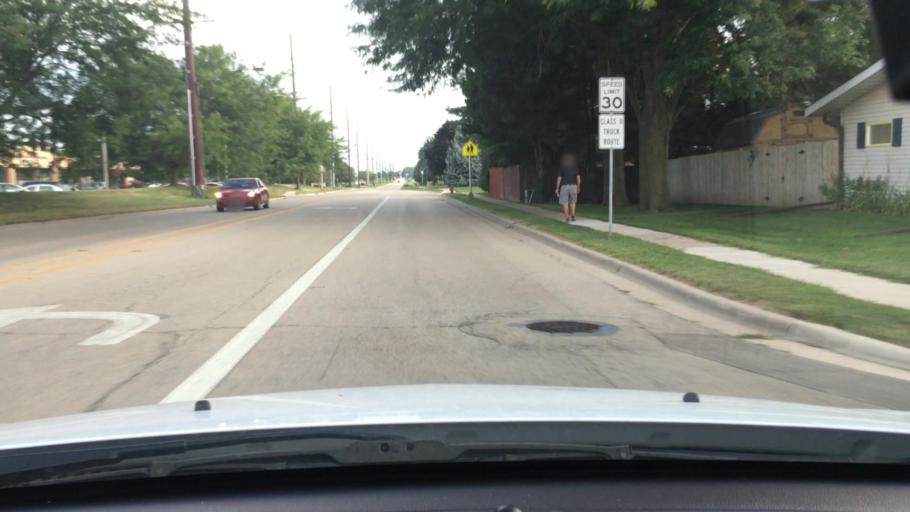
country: US
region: Illinois
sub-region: Ogle County
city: Rochelle
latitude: 41.9335
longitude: -89.0546
